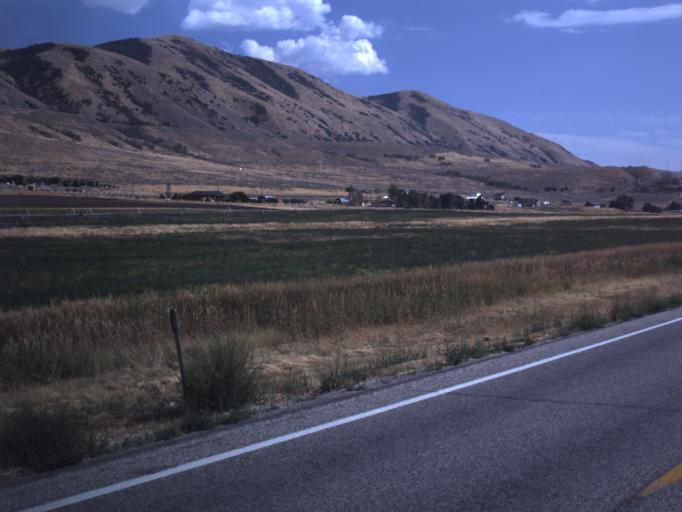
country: US
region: Utah
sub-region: Box Elder County
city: Garland
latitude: 41.7655
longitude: -112.0973
